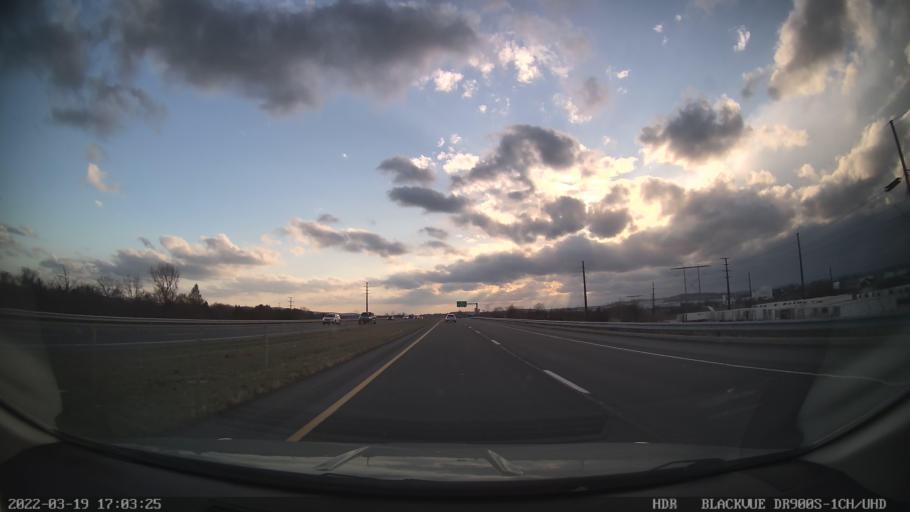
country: US
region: Pennsylvania
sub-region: Lehigh County
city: Trexlertown
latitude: 40.5633
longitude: -75.6003
